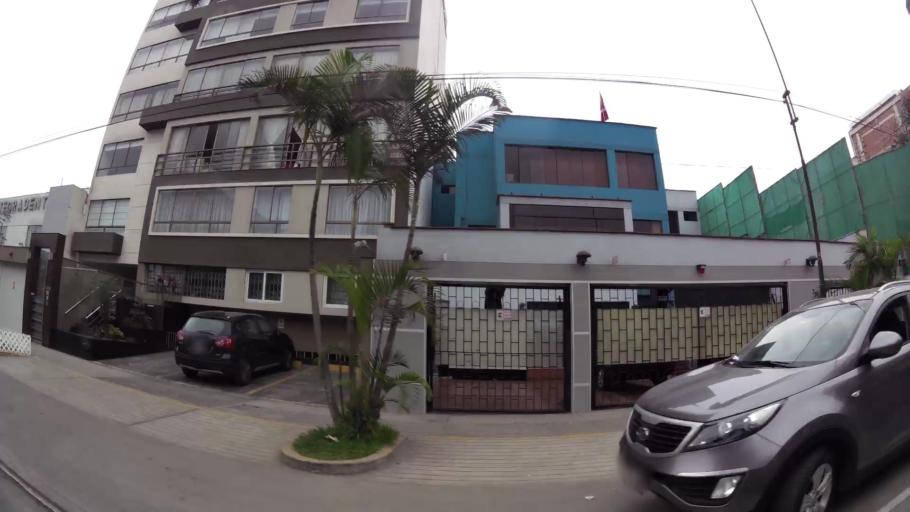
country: PE
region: Lima
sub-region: Lima
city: San Luis
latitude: -12.0922
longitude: -77.0091
